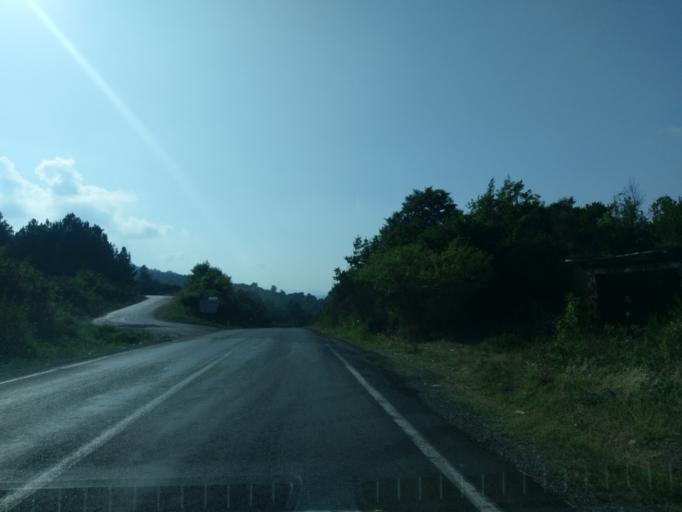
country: TR
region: Sinop
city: Yenikonak
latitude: 41.9427
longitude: 34.7003
